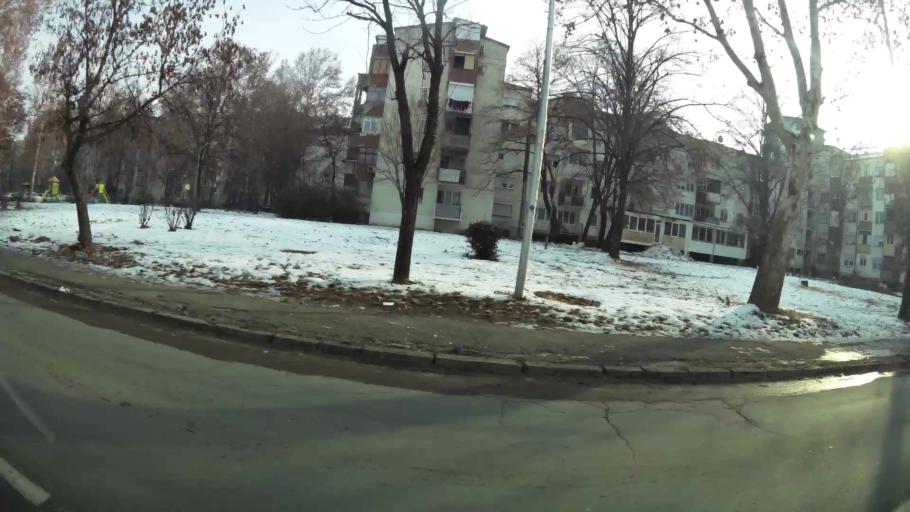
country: MK
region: Cair
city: Cair
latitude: 42.0158
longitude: 21.4311
